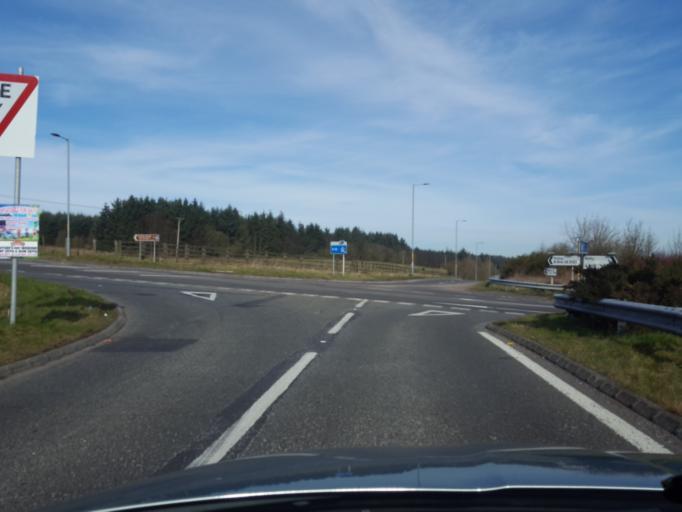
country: GB
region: Scotland
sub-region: Fife
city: Kelty
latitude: 56.1293
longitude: -3.3945
